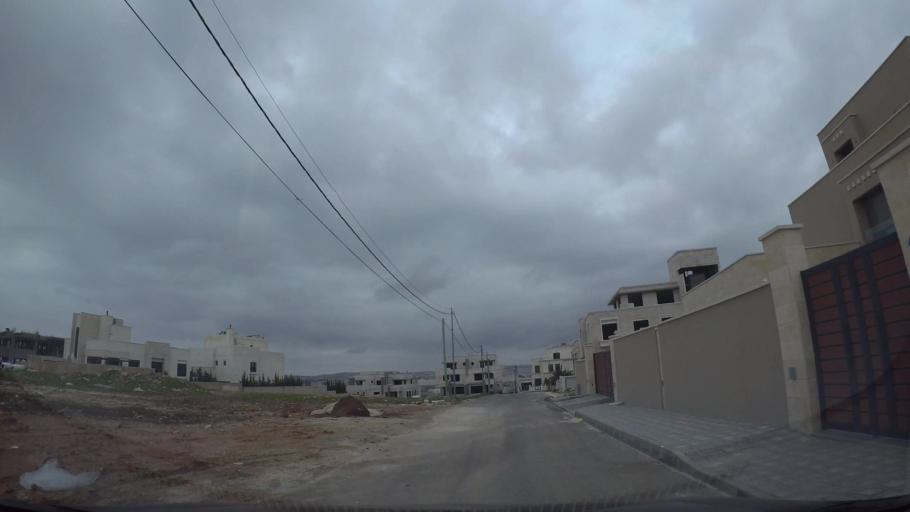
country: JO
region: Amman
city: Umm as Summaq
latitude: 31.9248
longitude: 35.8513
